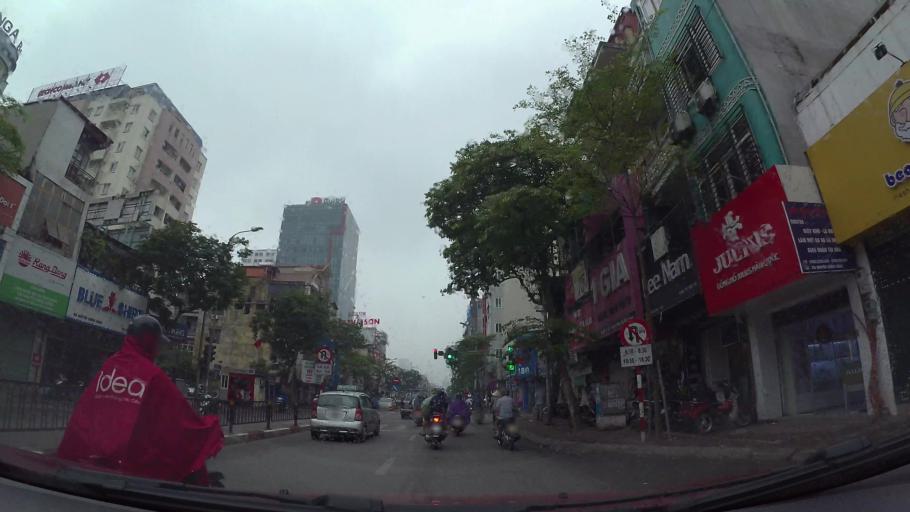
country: VN
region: Ha Noi
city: Dong Da
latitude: 21.0154
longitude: 105.8280
